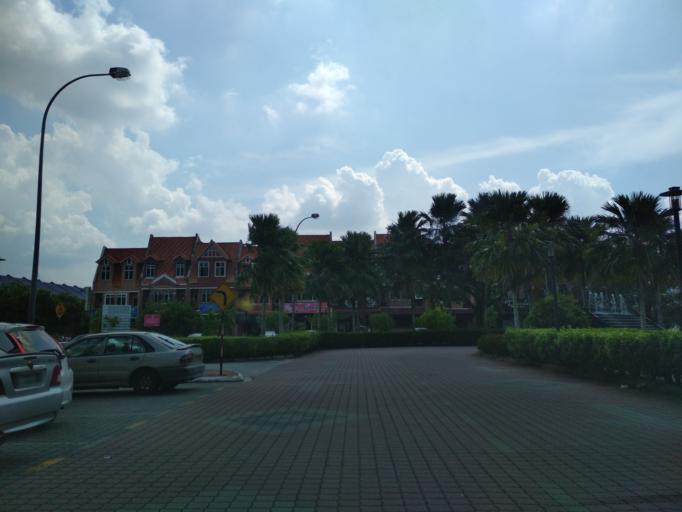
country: MY
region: Perak
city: Kampar
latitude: 4.3272
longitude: 101.1452
